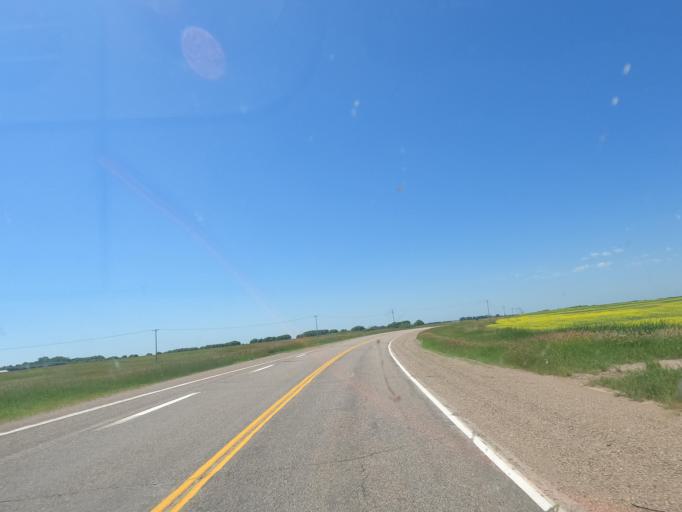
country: CA
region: Manitoba
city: Souris
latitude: 49.5855
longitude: -100.5354
